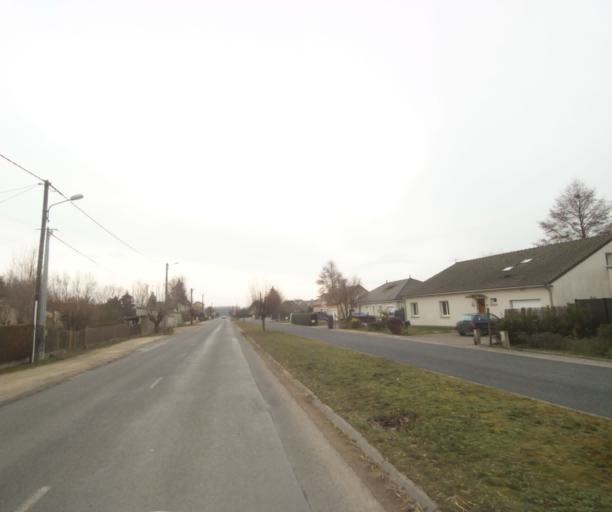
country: FR
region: Champagne-Ardenne
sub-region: Departement de la Haute-Marne
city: Villiers-en-Lieu
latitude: 48.6827
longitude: 4.8833
